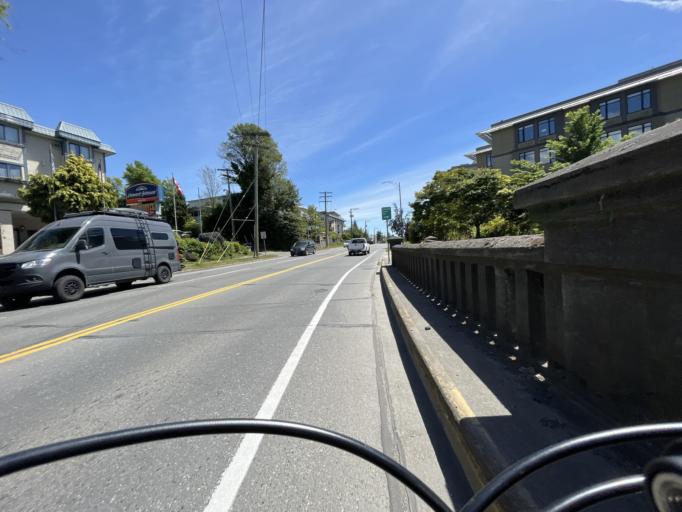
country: CA
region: British Columbia
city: Victoria
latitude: 48.4428
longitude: -123.3792
